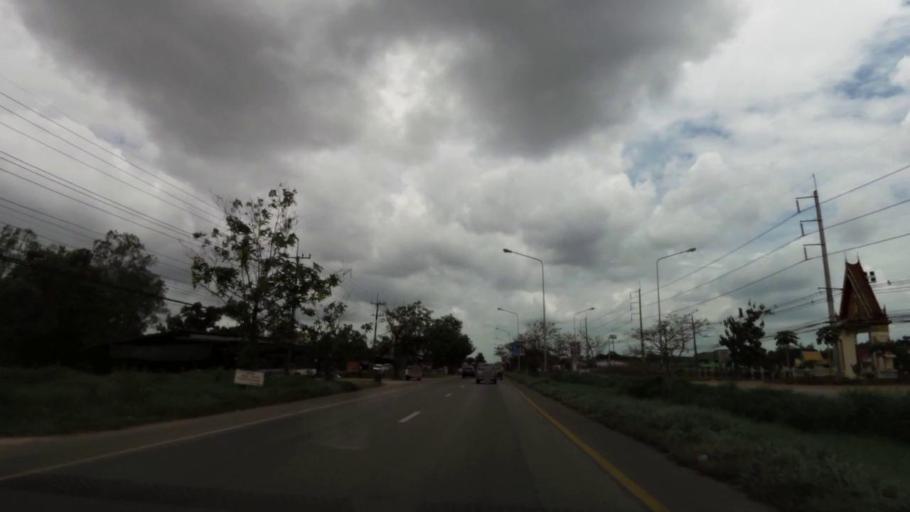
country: TH
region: Rayong
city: Klaeng
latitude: 12.7797
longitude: 101.7010
